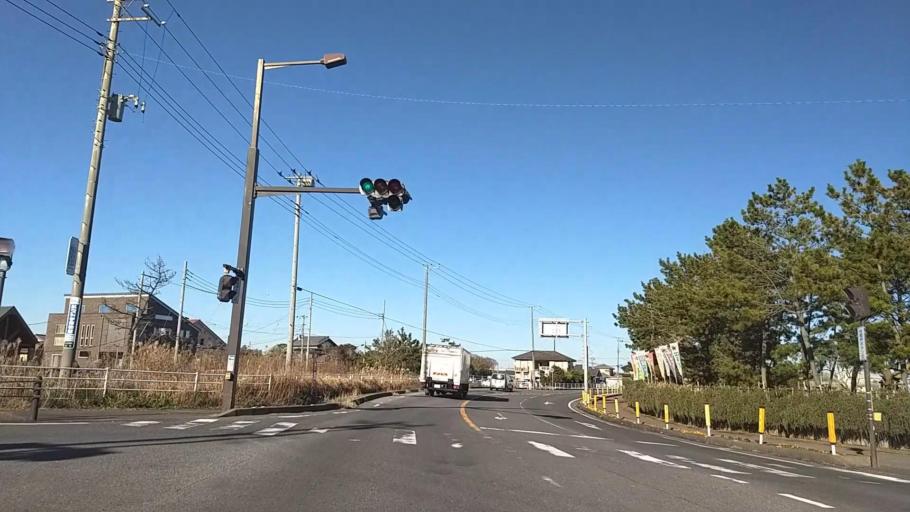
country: JP
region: Chiba
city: Togane
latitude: 35.5005
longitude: 140.4286
